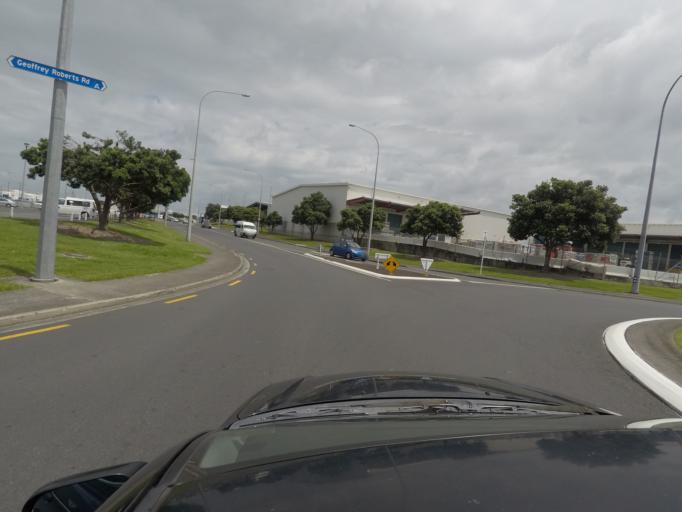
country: NZ
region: Auckland
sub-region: Auckland
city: Mangere
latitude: -37.0023
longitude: 174.7949
